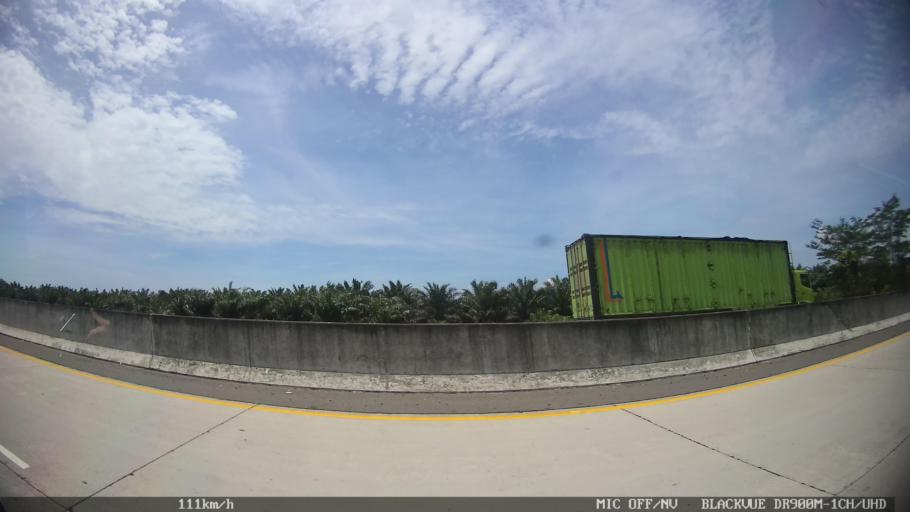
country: ID
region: North Sumatra
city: Perbaungan
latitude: 3.5324
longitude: 98.8736
